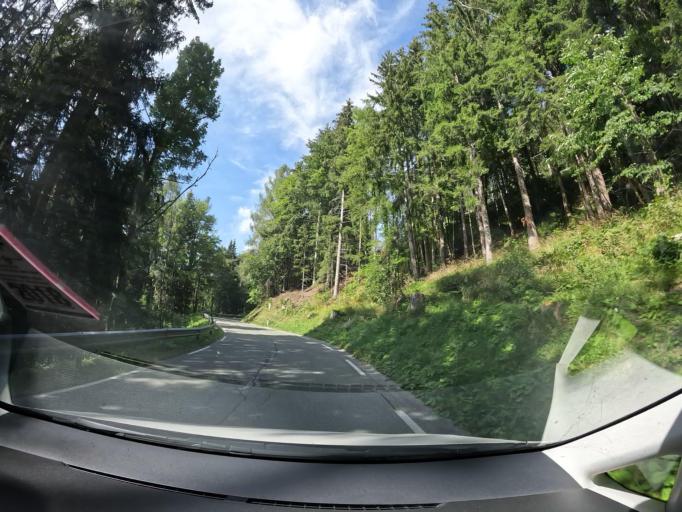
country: AT
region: Carinthia
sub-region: Politischer Bezirk Feldkirchen
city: Glanegg
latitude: 46.7341
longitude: 14.2146
